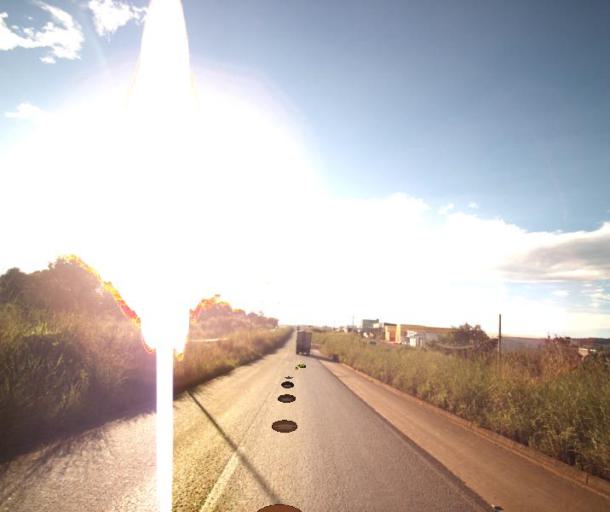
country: BR
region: Goias
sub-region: Anapolis
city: Anapolis
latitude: -16.2799
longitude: -48.9611
